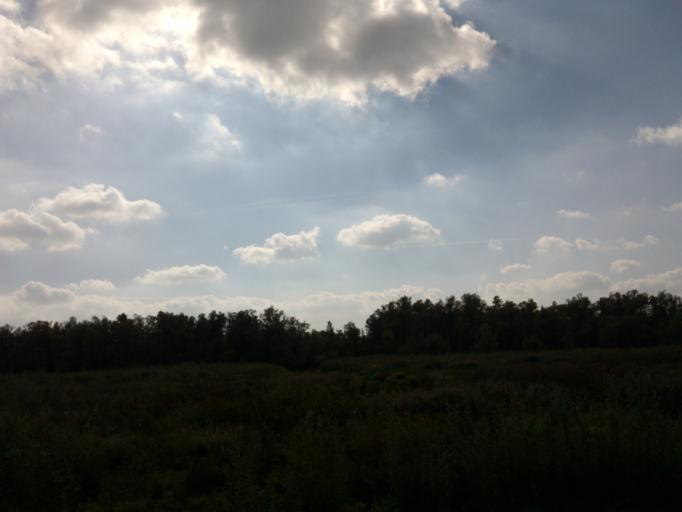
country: NL
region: North Brabant
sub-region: Gemeente Made en Drimmelen
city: Drimmelen
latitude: 51.7626
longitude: 4.8248
